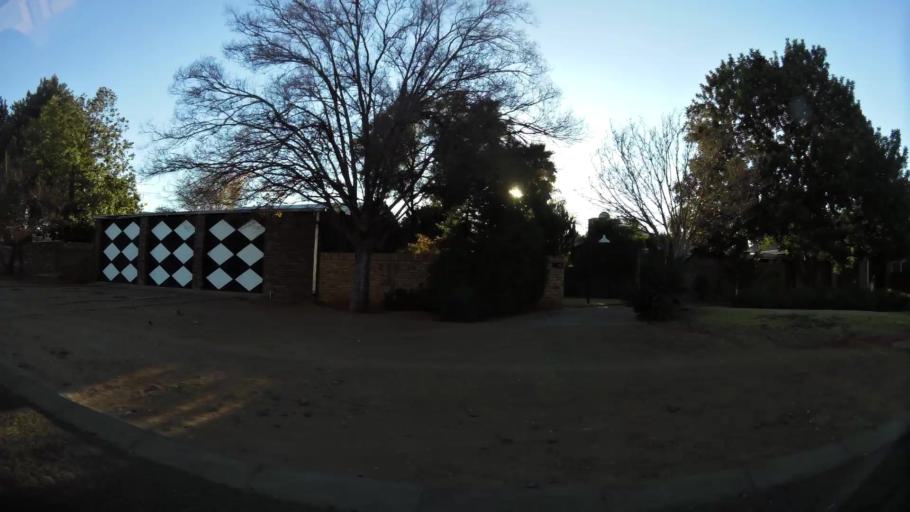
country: ZA
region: Northern Cape
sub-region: Frances Baard District Municipality
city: Kimberley
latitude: -28.7597
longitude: 24.7418
